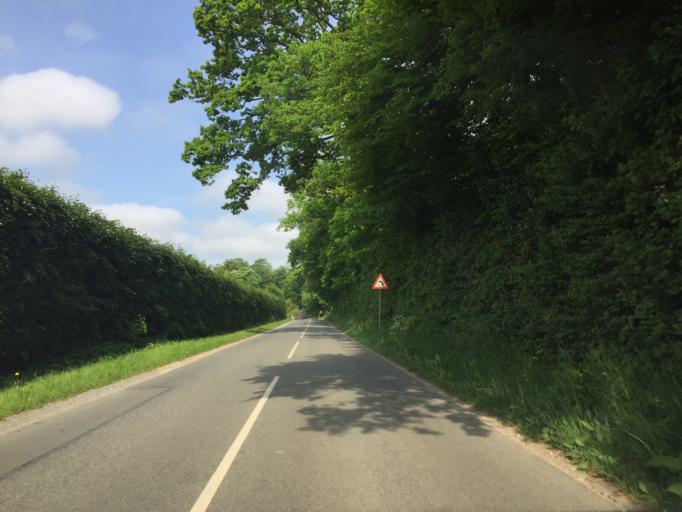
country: DK
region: South Denmark
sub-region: Svendborg Kommune
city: Thuro By
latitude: 55.1430
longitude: 10.7533
